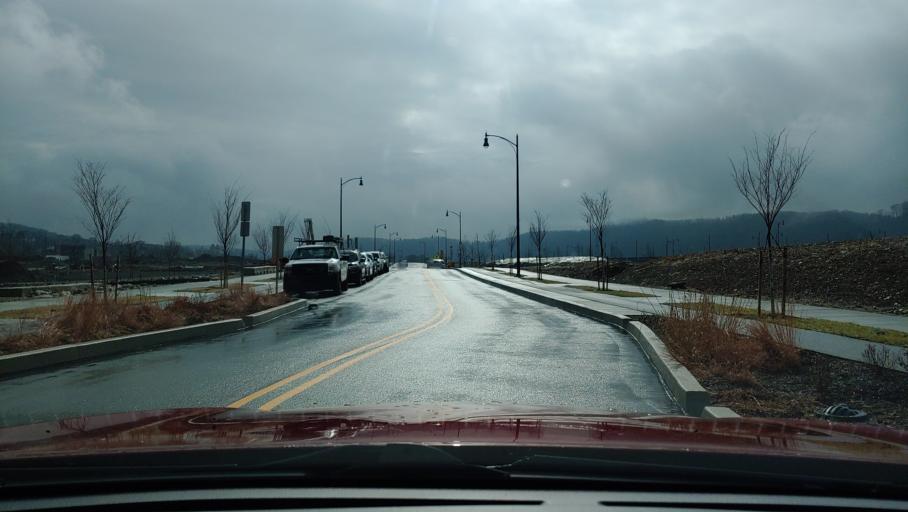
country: US
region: Pennsylvania
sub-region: Allegheny County
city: Homestead
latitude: 40.4146
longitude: -79.9484
